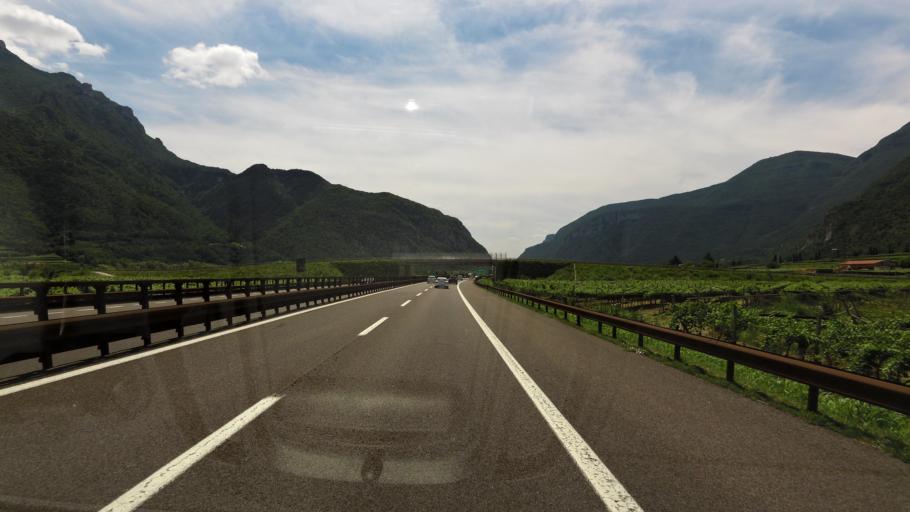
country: IT
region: Trentino-Alto Adige
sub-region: Provincia di Trento
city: Avio
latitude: 45.7010
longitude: 10.9220
